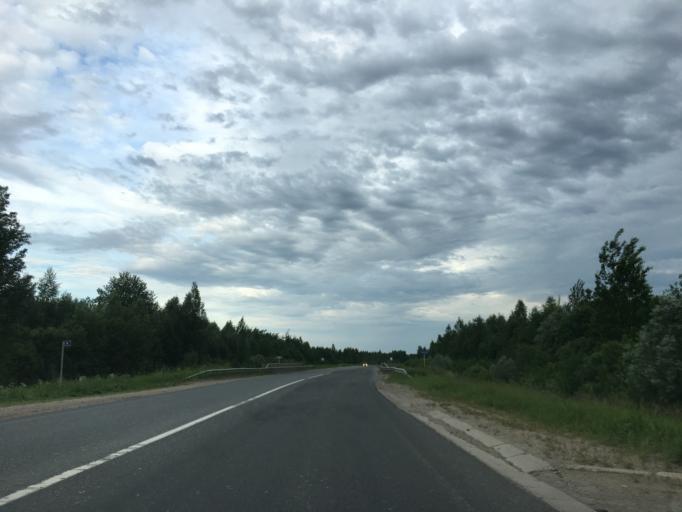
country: RU
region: Pskov
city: Pskov
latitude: 57.8569
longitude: 28.3677
